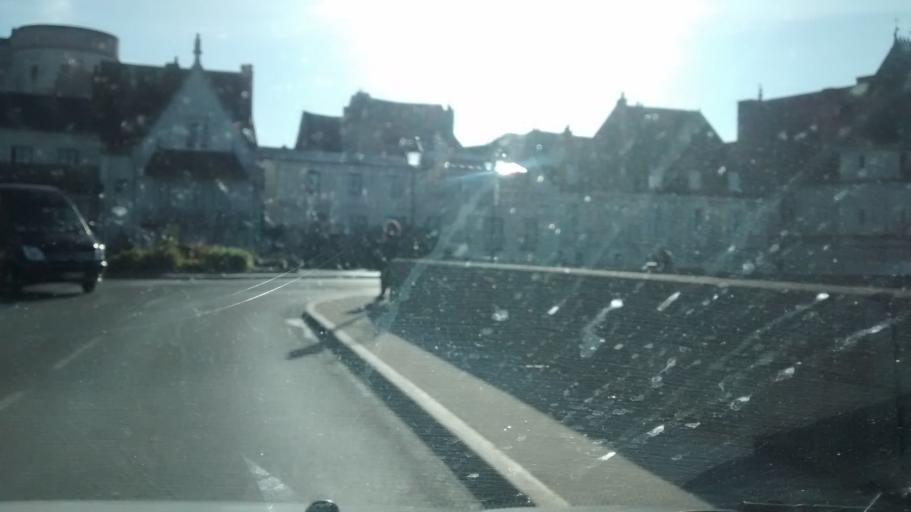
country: FR
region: Centre
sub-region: Departement d'Indre-et-Loire
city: Amboise
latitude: 47.4141
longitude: 0.9842
